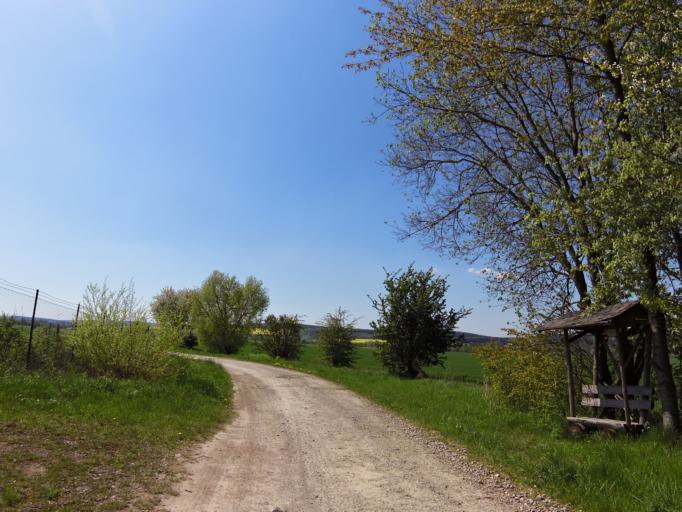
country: DE
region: Thuringia
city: Marksuhl
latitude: 50.8980
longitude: 10.2247
